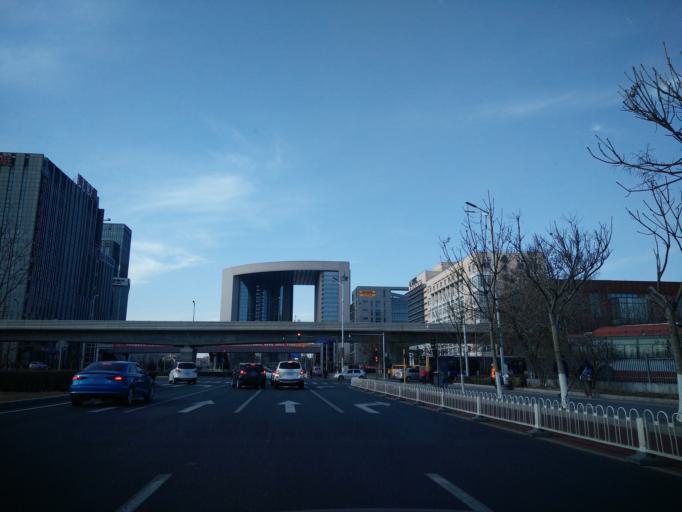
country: CN
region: Beijing
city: Jiugong
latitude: 39.7814
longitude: 116.5174
